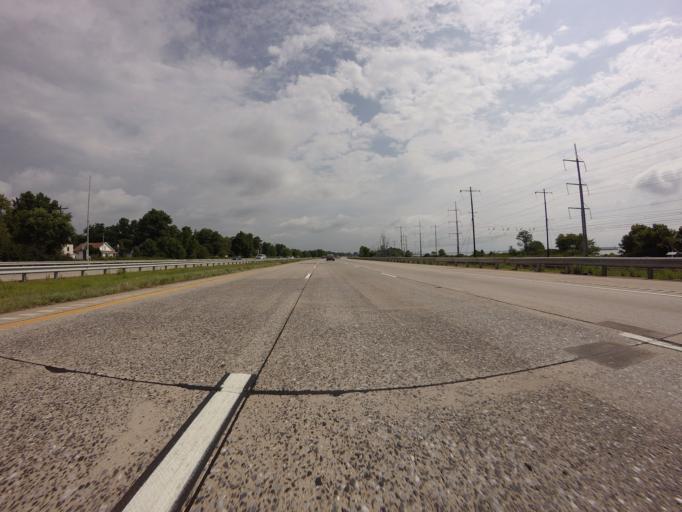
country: US
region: Delaware
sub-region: New Castle County
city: Claymont
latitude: 39.7879
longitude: -75.4682
